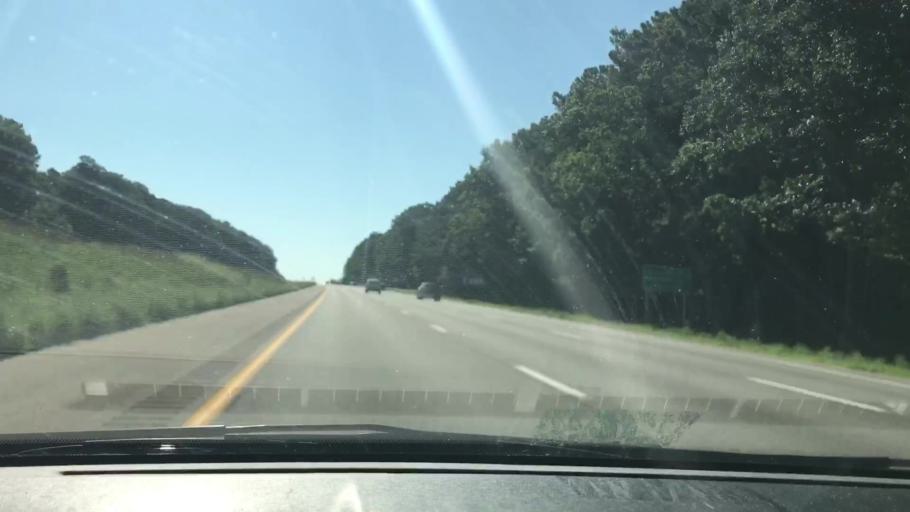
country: US
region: Virginia
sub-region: Henrico County
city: Tuckahoe
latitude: 37.6290
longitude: -77.5647
